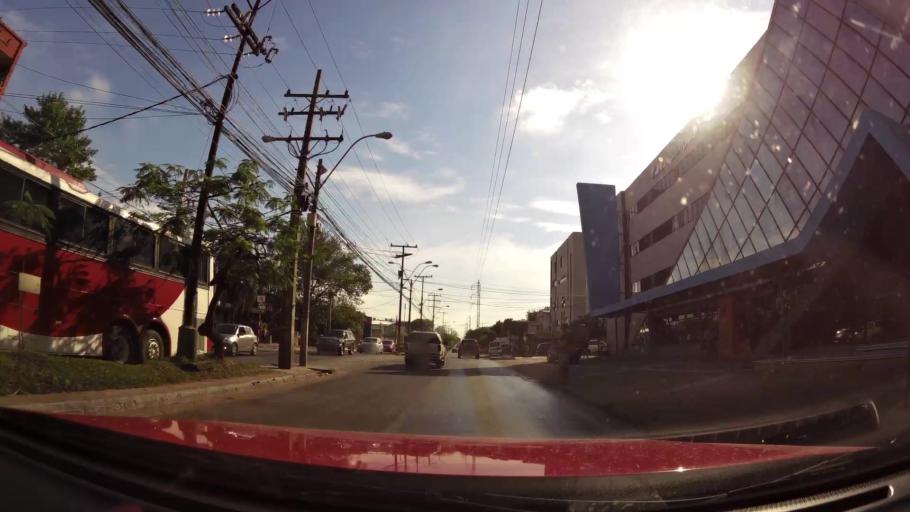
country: PY
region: Asuncion
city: Asuncion
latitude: -25.2696
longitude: -57.6018
